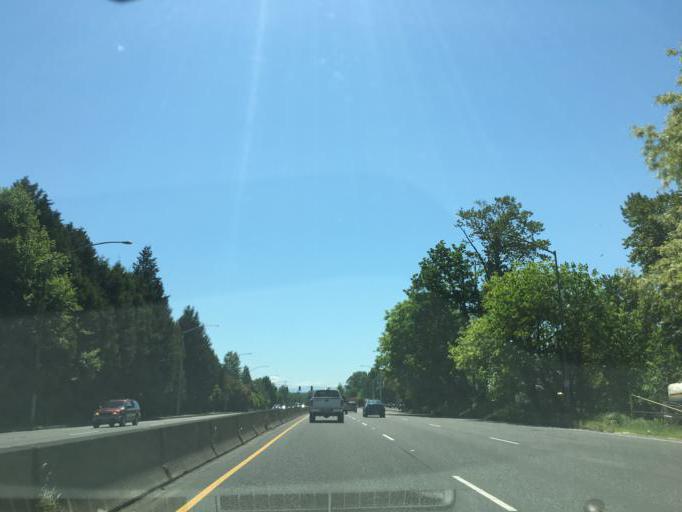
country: US
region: Oregon
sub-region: Multnomah County
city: Portland
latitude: 45.4943
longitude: -122.6576
